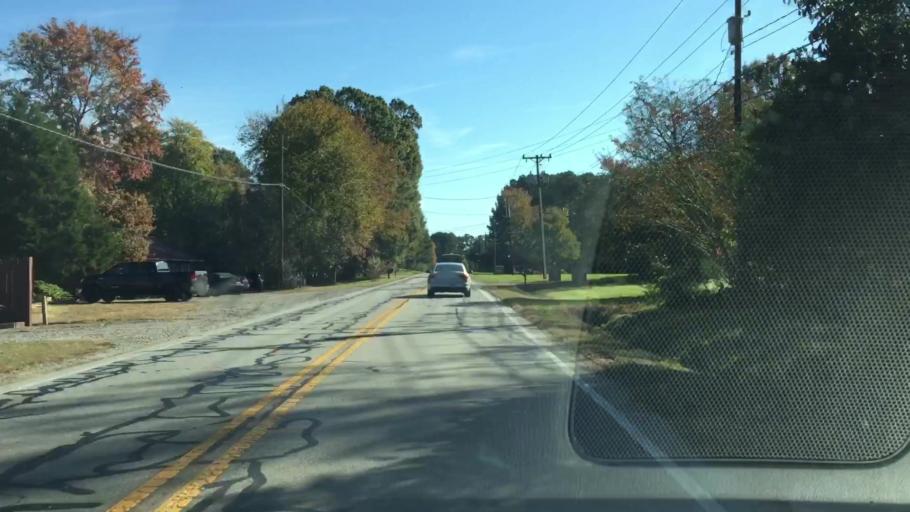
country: US
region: North Carolina
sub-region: Rowan County
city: Salisbury
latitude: 35.6614
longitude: -80.5544
